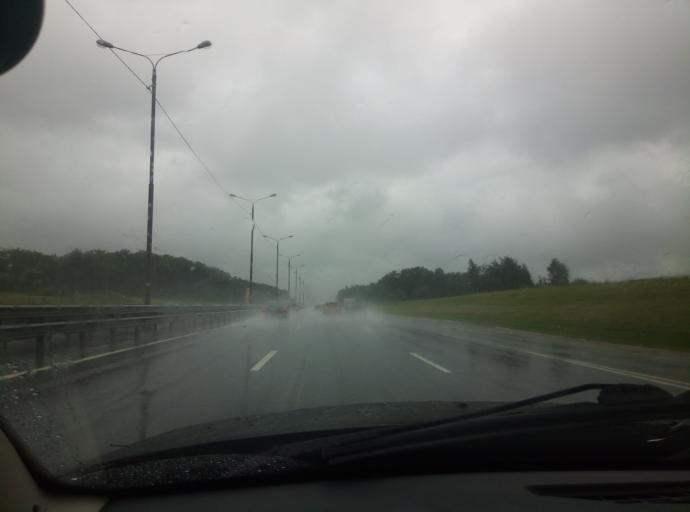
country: RU
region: Moskovskaya
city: Melikhovo
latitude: 55.1277
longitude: 37.5681
